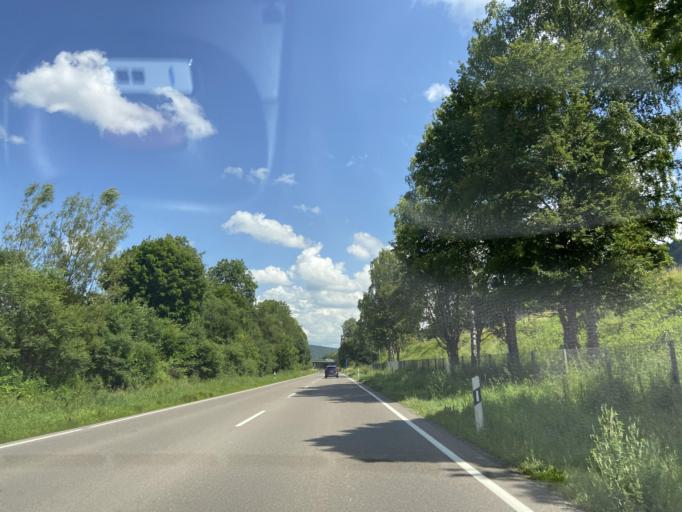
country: DE
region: Baden-Wuerttemberg
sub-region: Tuebingen Region
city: Albstadt
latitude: 48.2105
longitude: 8.9913
